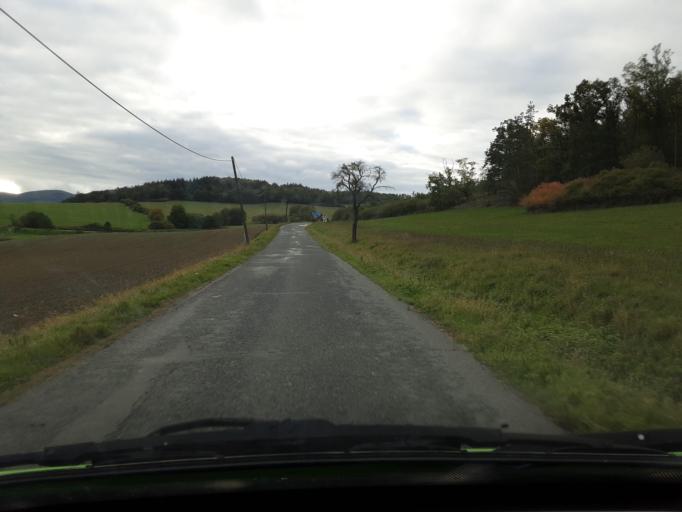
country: CZ
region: Plzensky
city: Janovice nad Uhlavou
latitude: 49.4281
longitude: 13.1675
